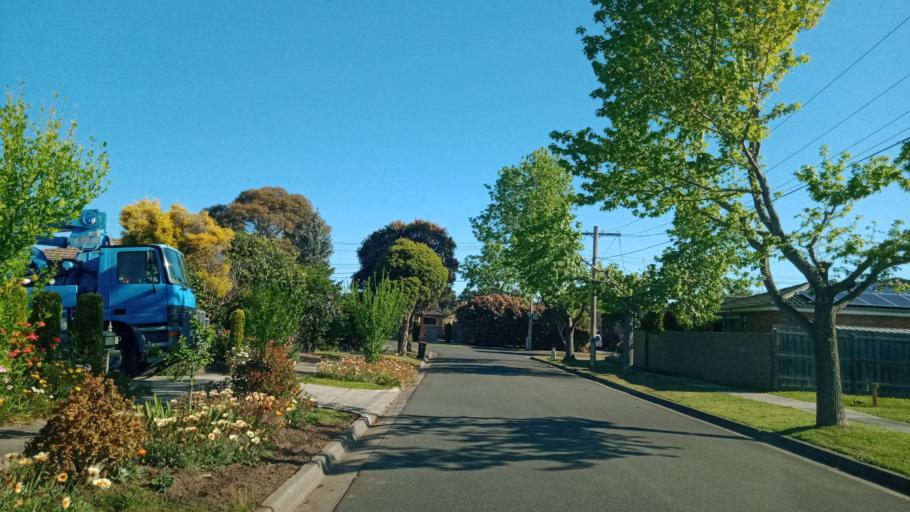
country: AU
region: Victoria
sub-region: Greater Dandenong
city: Noble Park North
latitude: -37.9343
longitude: 145.1837
